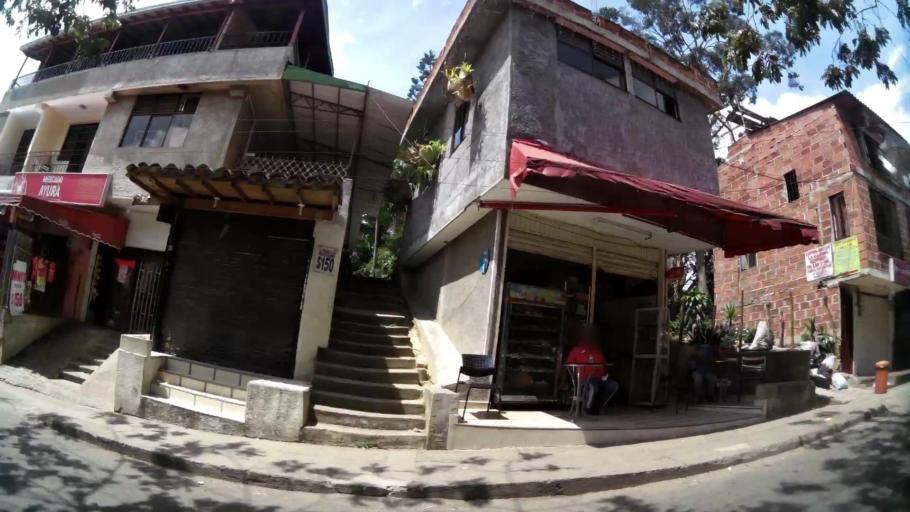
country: CO
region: Antioquia
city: Bello
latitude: 6.3481
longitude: -75.5511
